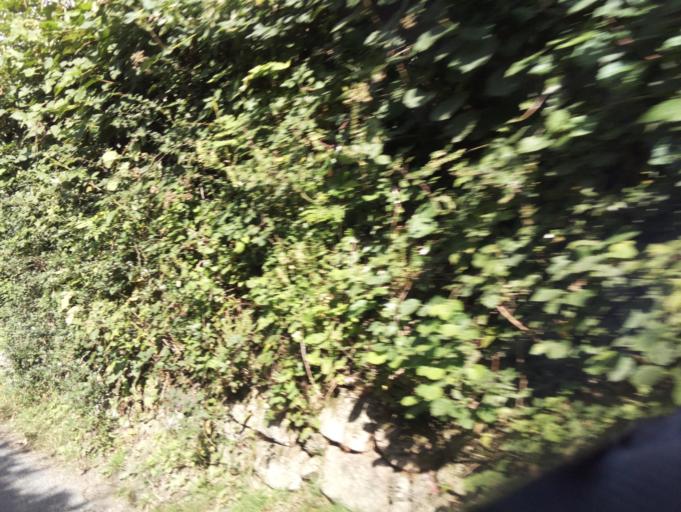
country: GB
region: England
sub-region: Devon
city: Buckfastleigh
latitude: 50.5351
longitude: -3.8285
